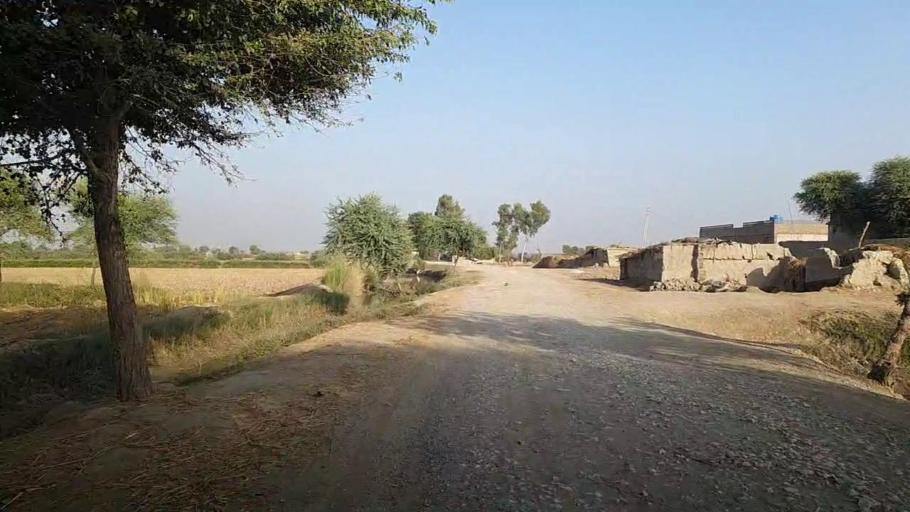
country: PK
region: Sindh
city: Kashmor
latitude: 28.4267
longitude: 69.4365
